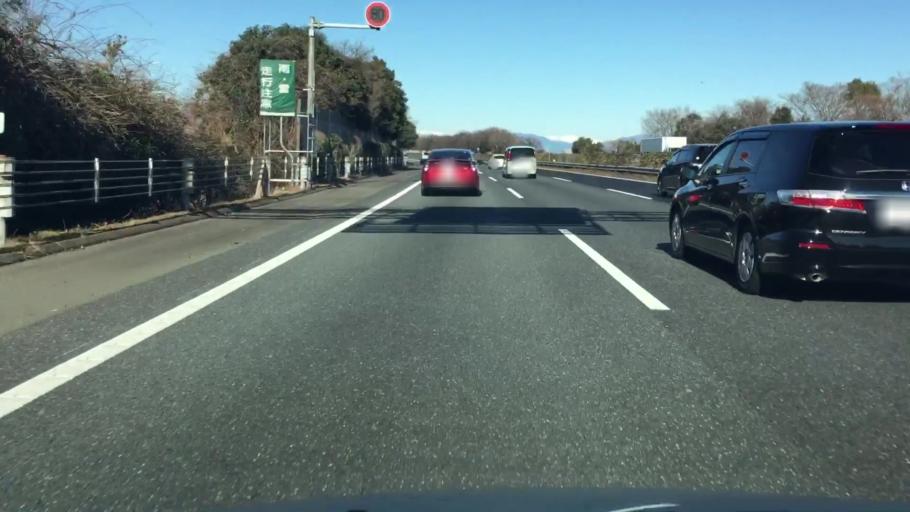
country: JP
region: Saitama
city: Honjo
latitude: 36.2428
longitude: 139.1439
